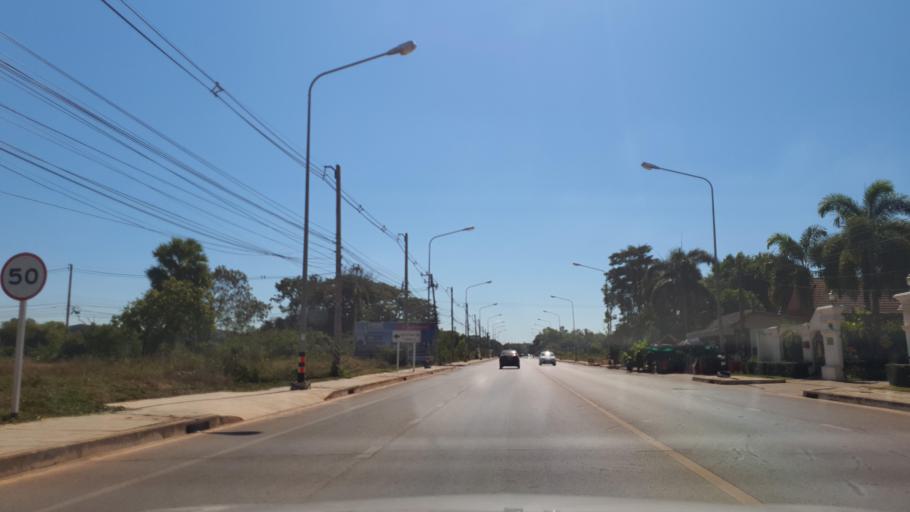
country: TH
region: Sakon Nakhon
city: Sakon Nakhon
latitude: 17.1520
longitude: 104.1282
